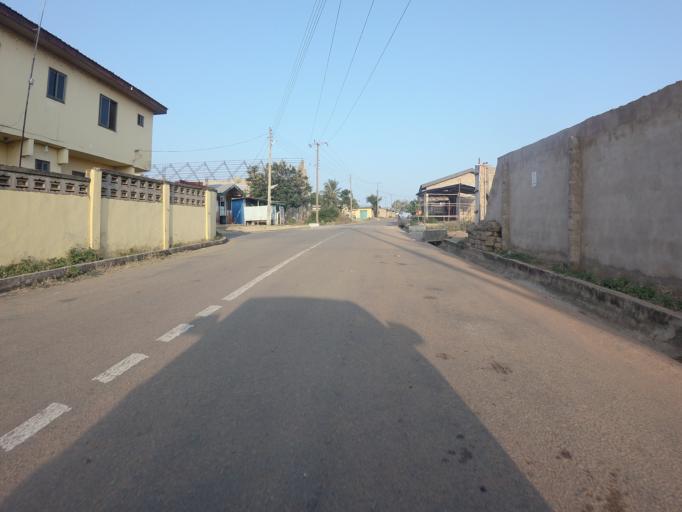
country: GH
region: Volta
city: Anloga
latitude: 6.0054
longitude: 0.5955
